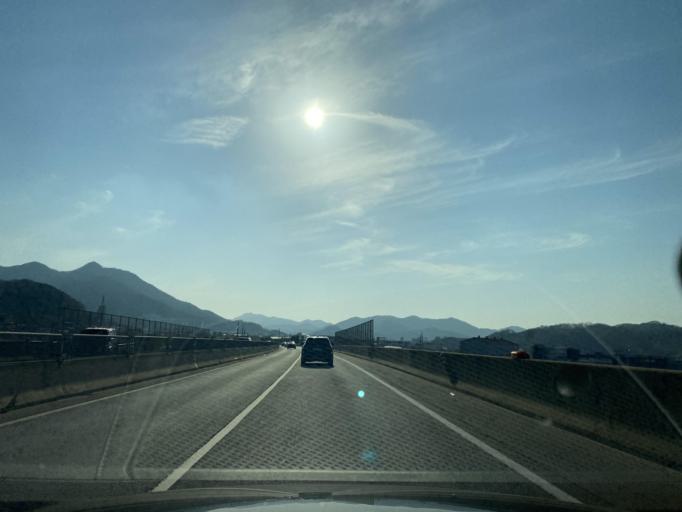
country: KR
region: Chungcheongnam-do
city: Asan
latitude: 36.7716
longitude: 127.0414
